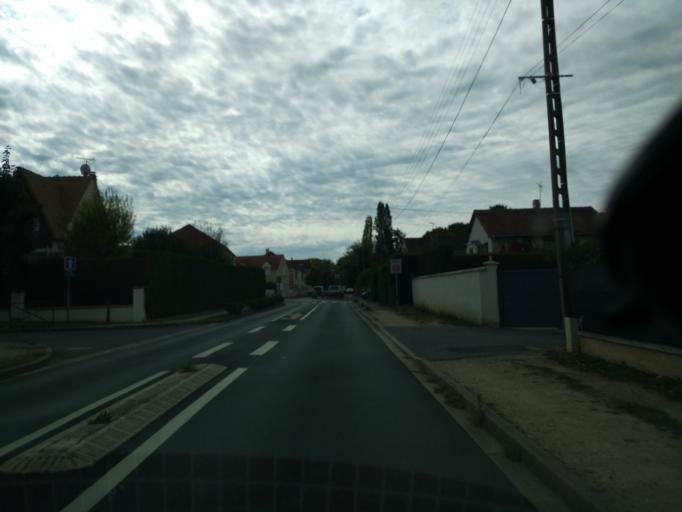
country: FR
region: Ile-de-France
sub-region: Departement de l'Essonne
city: Les Molieres
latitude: 48.6757
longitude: 2.0711
